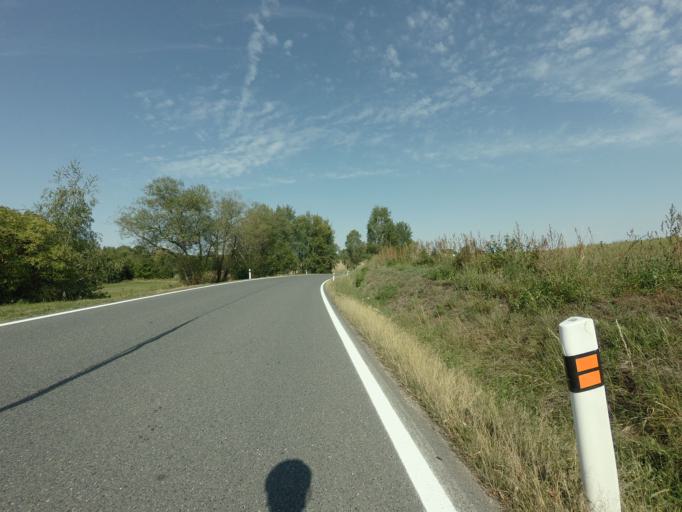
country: CZ
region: Jihocesky
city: Bernartice
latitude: 49.3833
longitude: 14.3630
